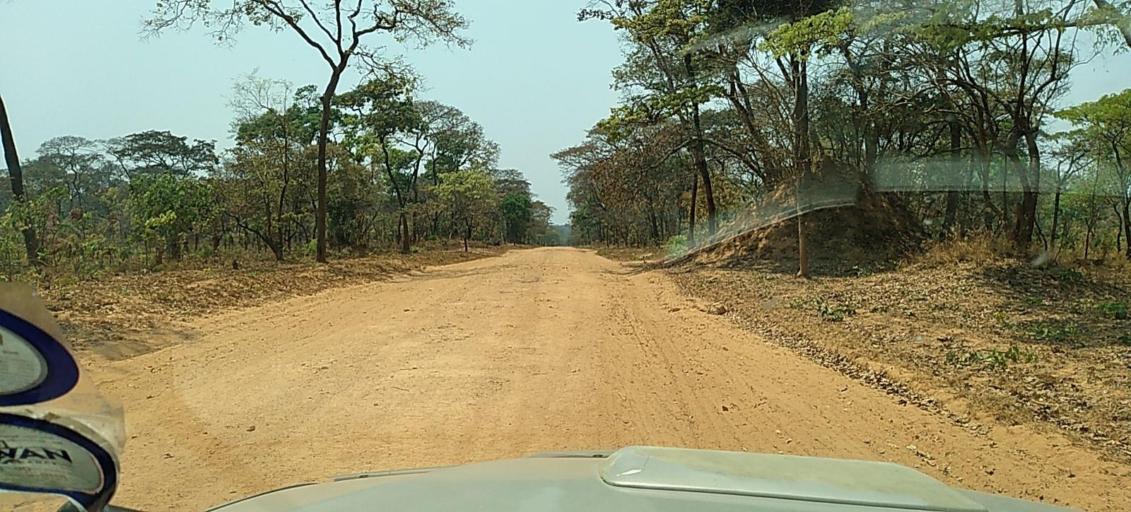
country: ZM
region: North-Western
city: Kasempa
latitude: -13.5475
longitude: 26.0347
